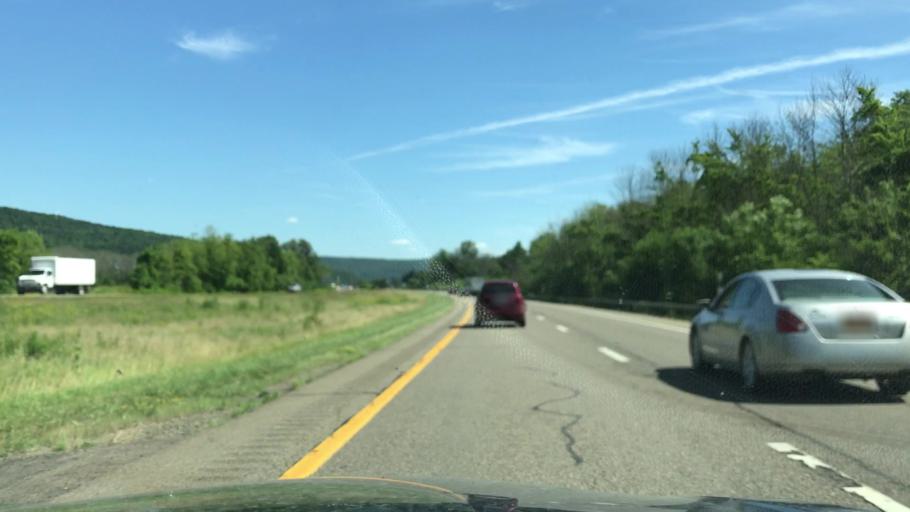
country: US
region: New York
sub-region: Steuben County
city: Gang Mills
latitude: 42.2164
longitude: -77.1773
